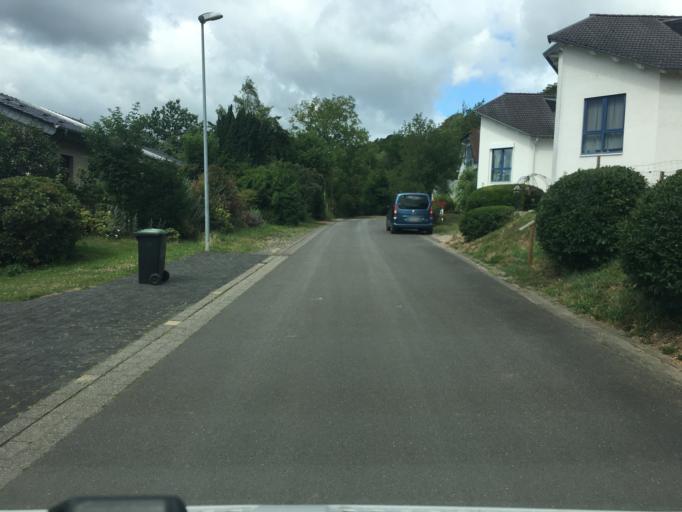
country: DE
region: North Rhine-Westphalia
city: Heimbach
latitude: 50.6410
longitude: 6.4570
